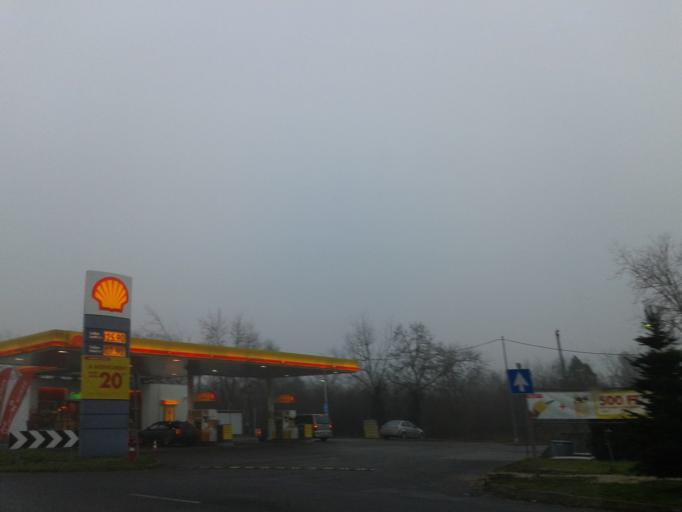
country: HU
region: Budapest
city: Budapest XXII. keruelet
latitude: 47.4360
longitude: 19.0068
